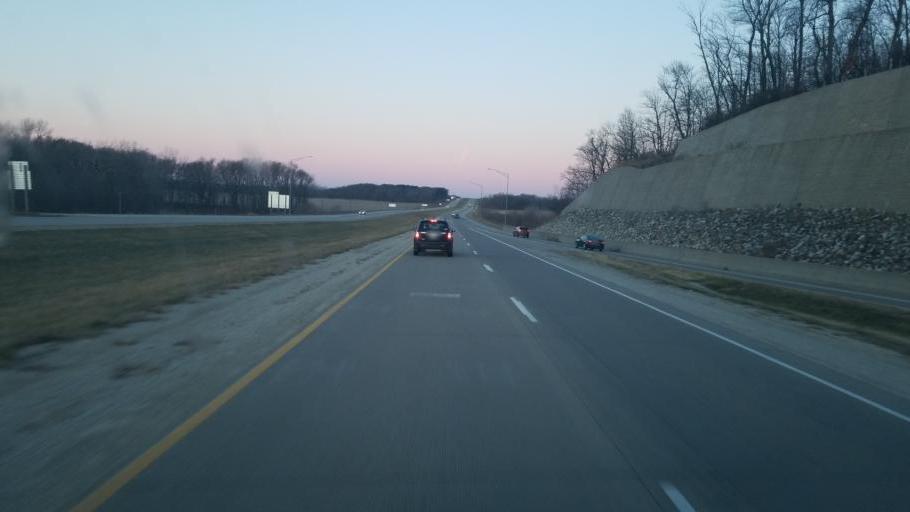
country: US
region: Iowa
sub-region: Henry County
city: Mount Pleasant
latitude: 40.9699
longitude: -91.6381
